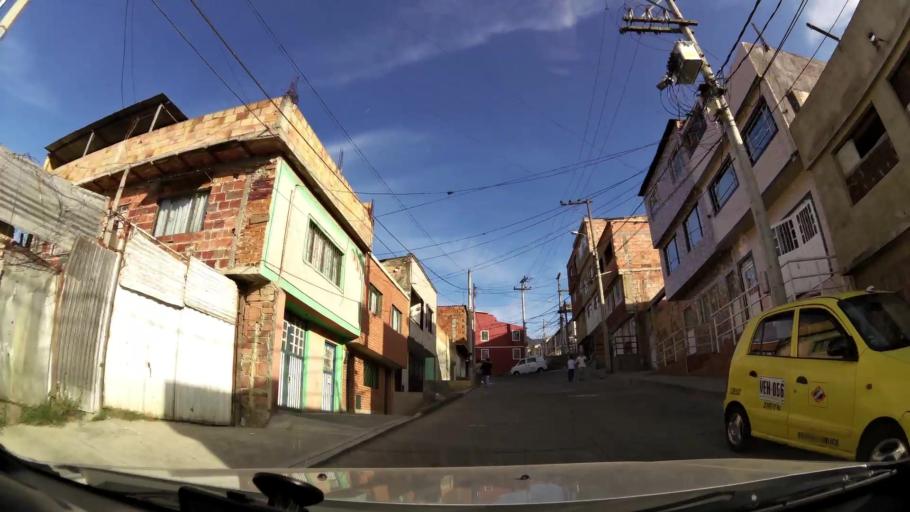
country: CO
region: Bogota D.C.
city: Bogota
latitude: 4.5420
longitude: -74.0927
